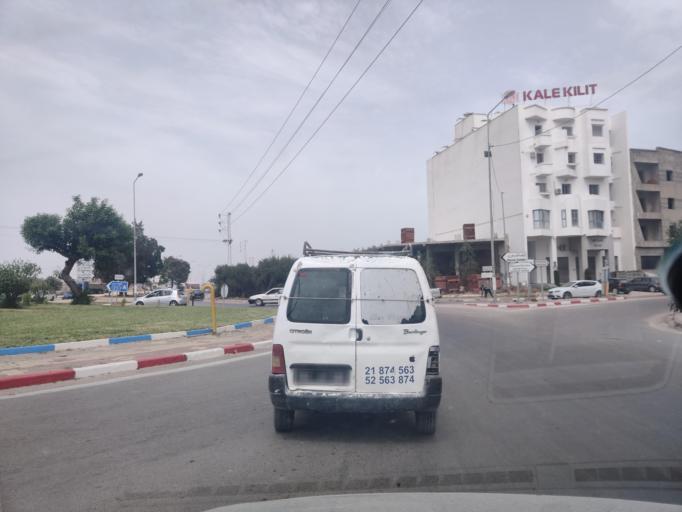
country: TN
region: Susah
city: Hammam Sousse
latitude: 35.8401
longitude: 10.5839
